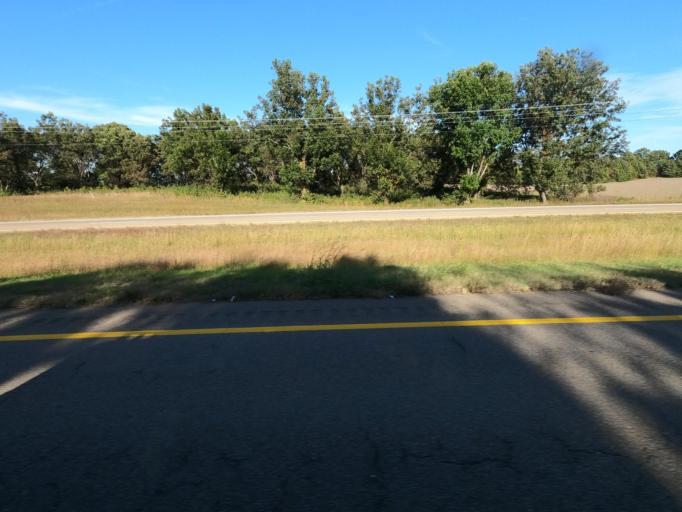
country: US
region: Tennessee
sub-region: Lauderdale County
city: Halls
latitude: 35.8938
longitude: -89.2397
